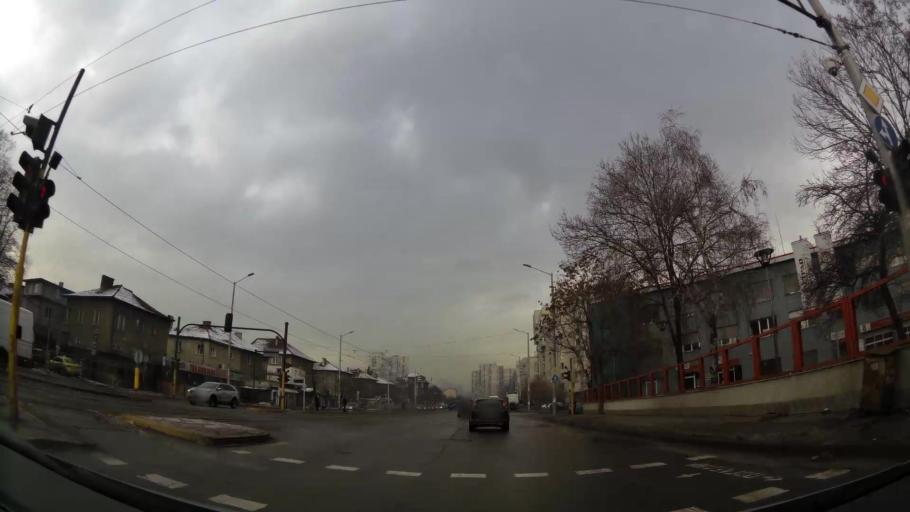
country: BG
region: Sofia-Capital
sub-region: Stolichna Obshtina
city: Sofia
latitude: 42.6945
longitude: 23.2927
